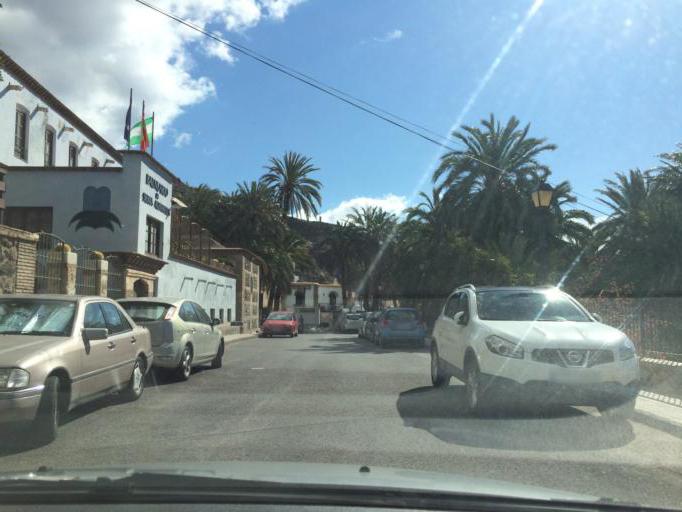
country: ES
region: Andalusia
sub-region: Provincia de Almeria
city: Pechina
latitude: 36.9608
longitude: -2.3972
